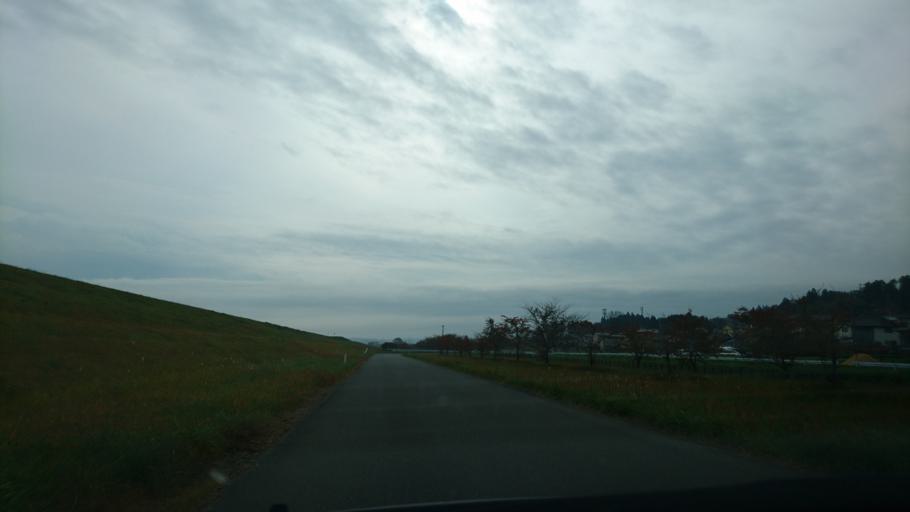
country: JP
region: Iwate
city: Ichinoseki
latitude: 38.9579
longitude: 141.1303
